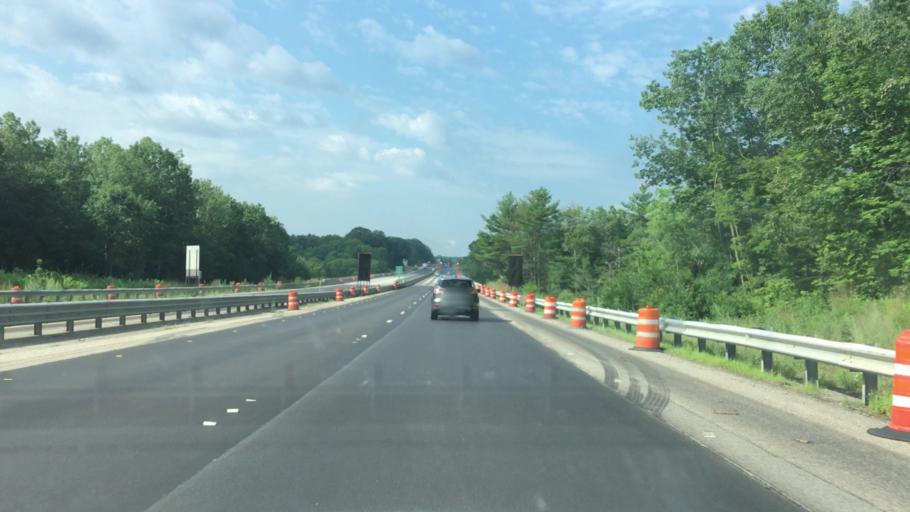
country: US
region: Maine
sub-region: Androscoggin County
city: Lewiston
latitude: 44.0666
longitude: -70.2051
